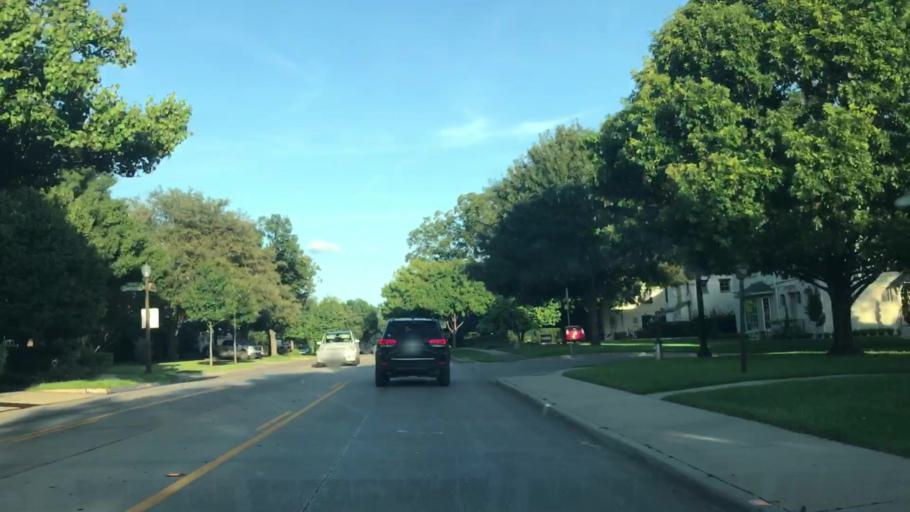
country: US
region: Texas
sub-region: Dallas County
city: Highland Park
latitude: 32.8511
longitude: -96.7756
